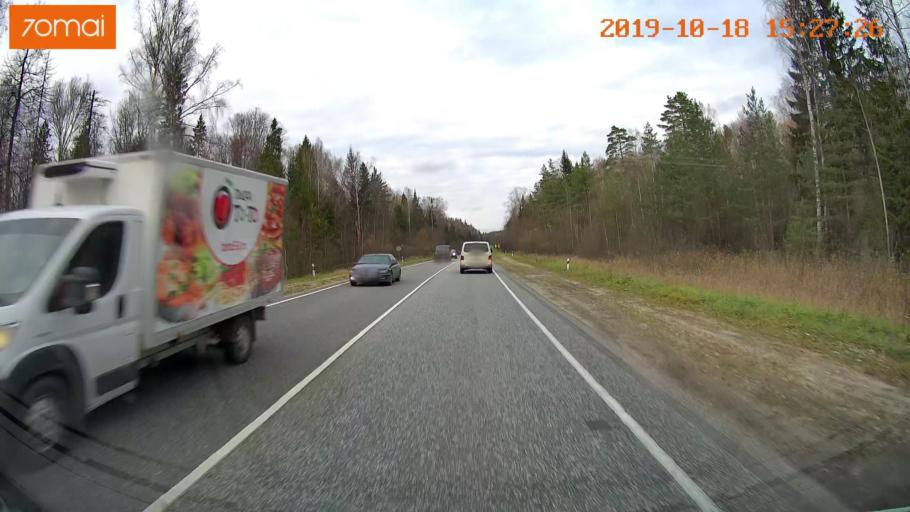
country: RU
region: Vladimir
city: Anopino
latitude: 55.7531
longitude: 40.6711
